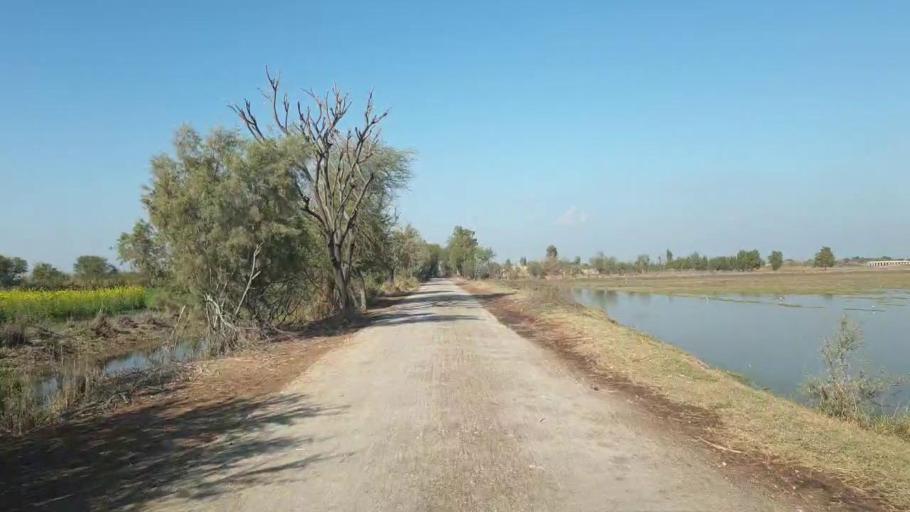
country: PK
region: Sindh
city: Shahdadpur
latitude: 25.9233
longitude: 68.5301
